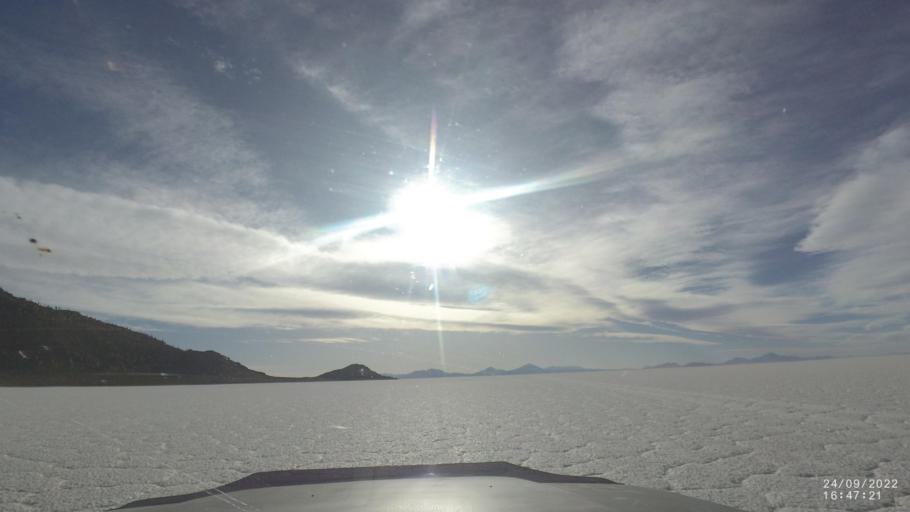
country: BO
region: Potosi
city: Colchani
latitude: -20.1324
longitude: -67.8015
